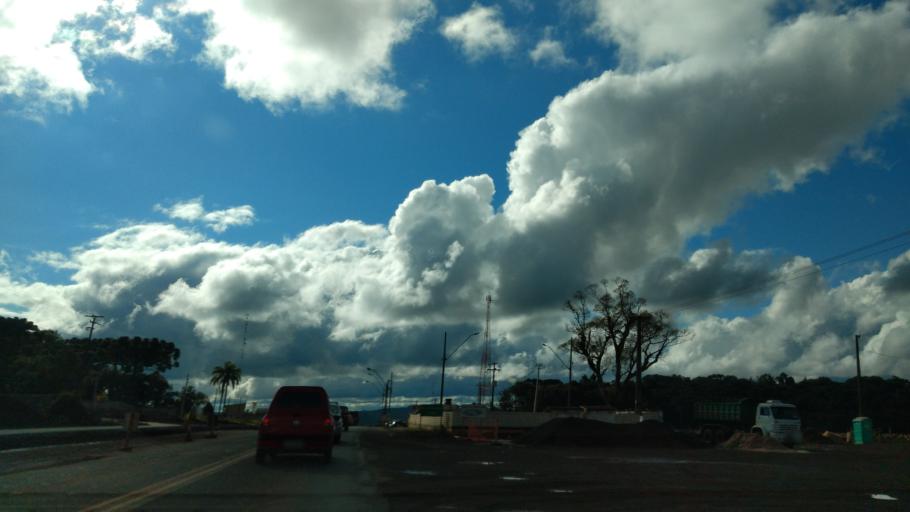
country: BR
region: Parana
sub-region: Guarapuava
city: Guarapuava
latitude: -25.3434
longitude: -51.4912
